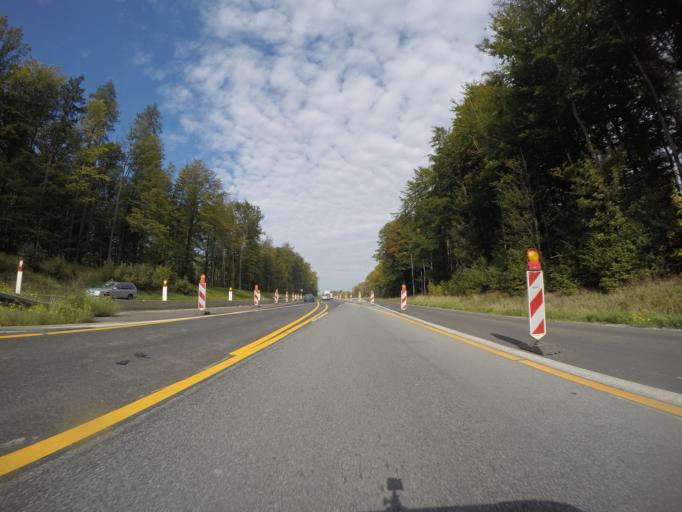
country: DE
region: Bavaria
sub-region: Regierungsbezirk Unterfranken
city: Weibersbrunn
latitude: 49.9107
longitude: 9.3688
